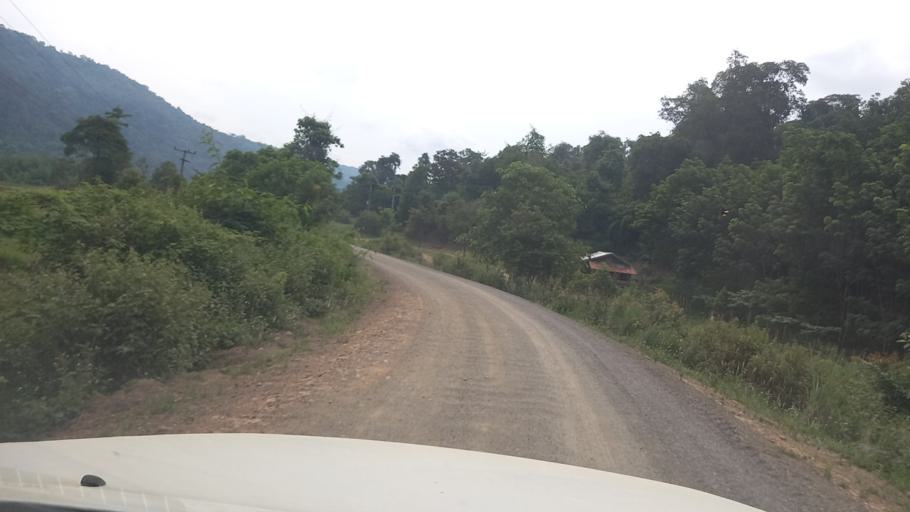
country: LA
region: Bolikhamxai
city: Ban Nahin
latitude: 18.1493
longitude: 104.7399
